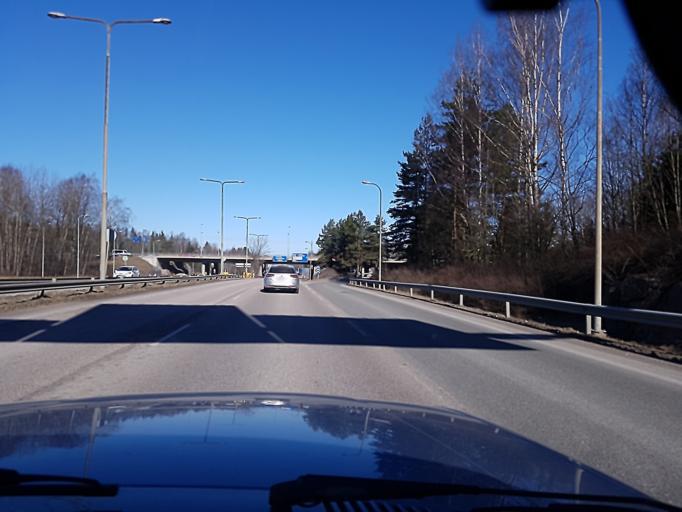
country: FI
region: Uusimaa
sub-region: Helsinki
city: Helsinki
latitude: 60.2338
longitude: 24.9013
